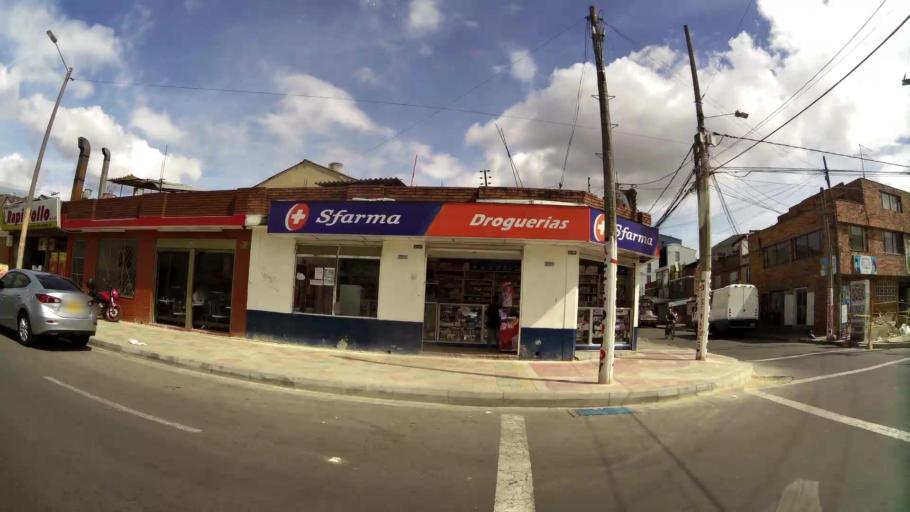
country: CO
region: Bogota D.C.
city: Bogota
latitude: 4.6168
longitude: -74.1304
